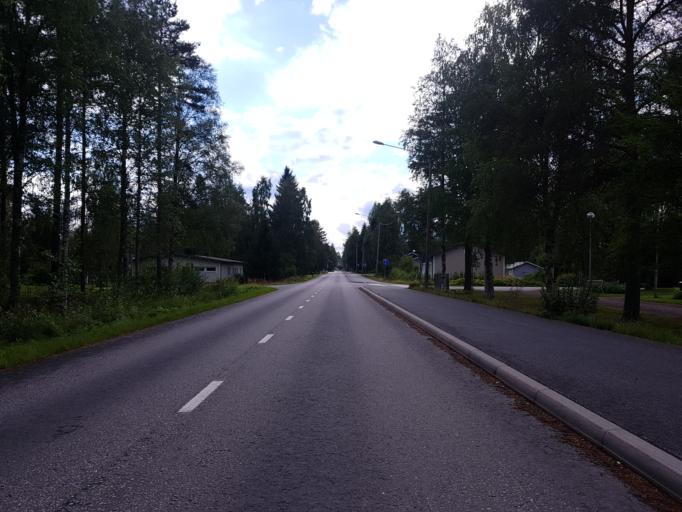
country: FI
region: Kainuu
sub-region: Kehys-Kainuu
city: Kuhmo
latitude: 64.1255
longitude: 29.5362
